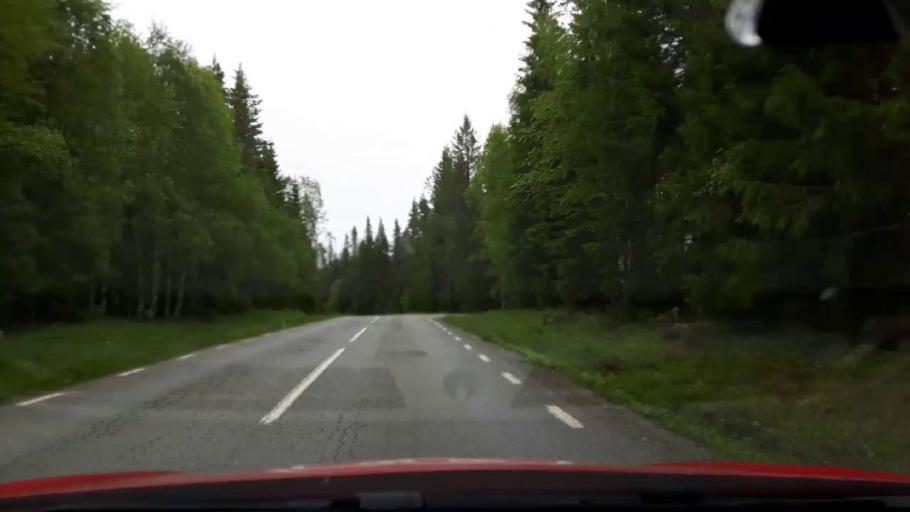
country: SE
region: Jaemtland
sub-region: Stroemsunds Kommun
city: Stroemsund
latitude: 63.4488
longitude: 15.4700
